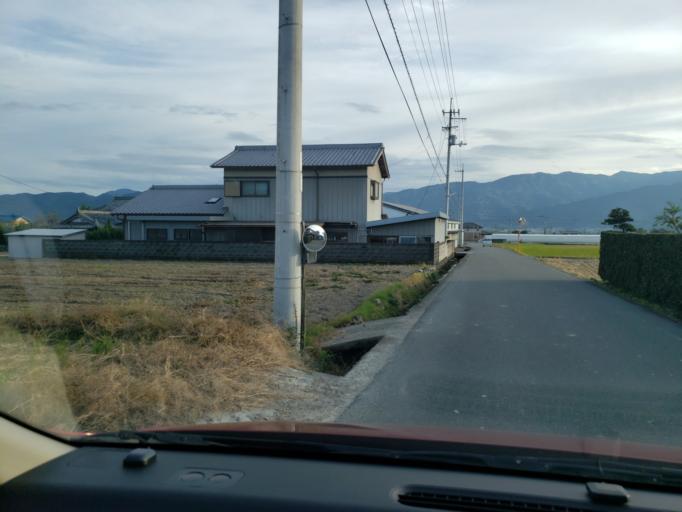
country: JP
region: Tokushima
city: Wakimachi
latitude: 34.0850
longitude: 134.2269
